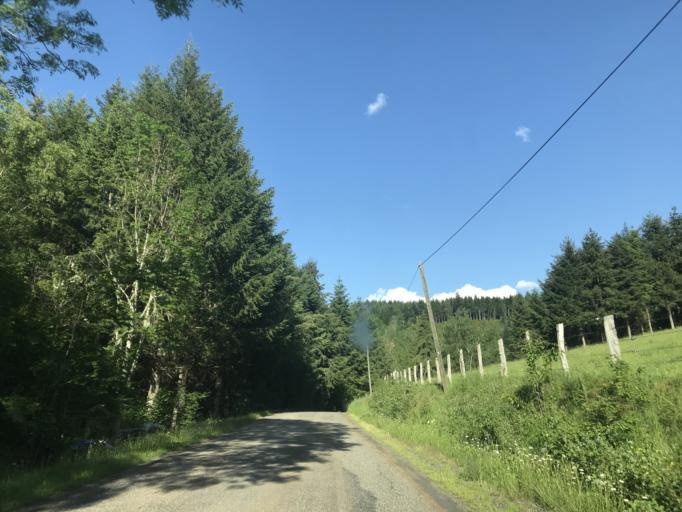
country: FR
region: Auvergne
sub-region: Departement du Puy-de-Dome
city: Job
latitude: 45.6105
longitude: 3.6627
